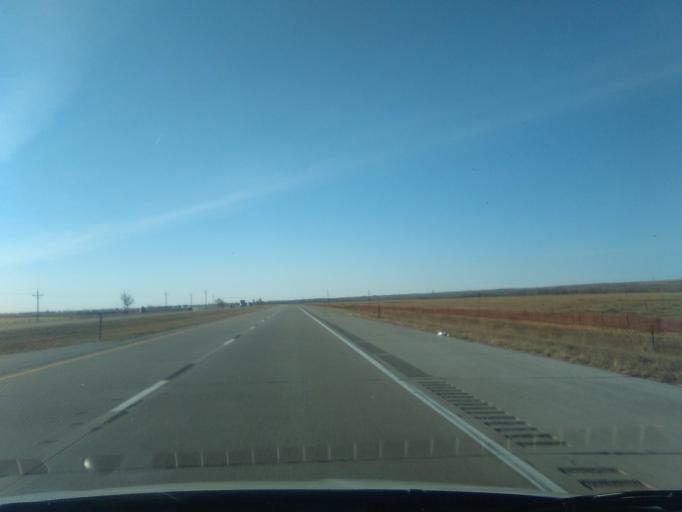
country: US
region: Colorado
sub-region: Sedgwick County
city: Julesburg
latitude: 41.0626
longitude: -102.0102
